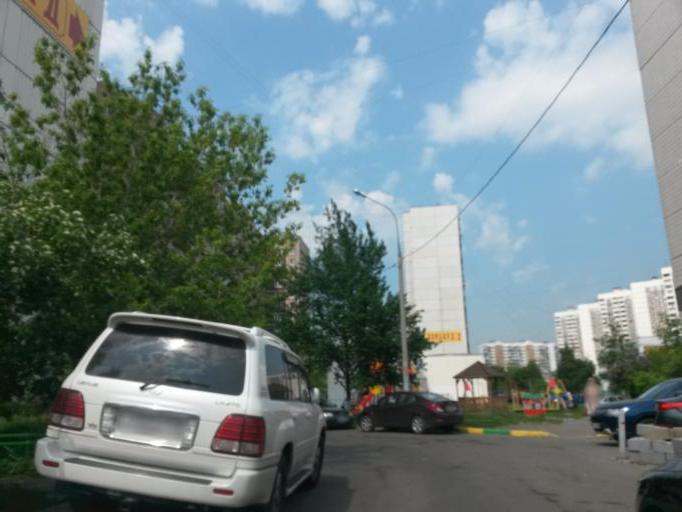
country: RU
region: Moscow
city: Mar'ino
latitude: 55.6481
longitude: 37.7389
